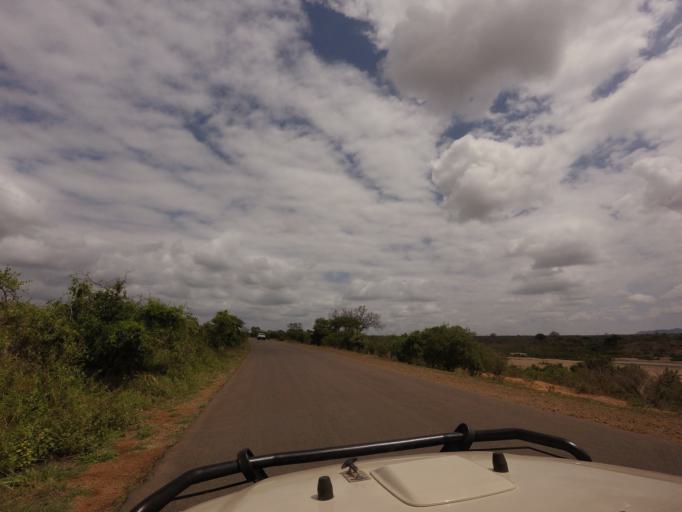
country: ZA
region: Mpumalanga
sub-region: Ehlanzeni District
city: Komatipoort
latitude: -25.1059
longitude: 31.9020
